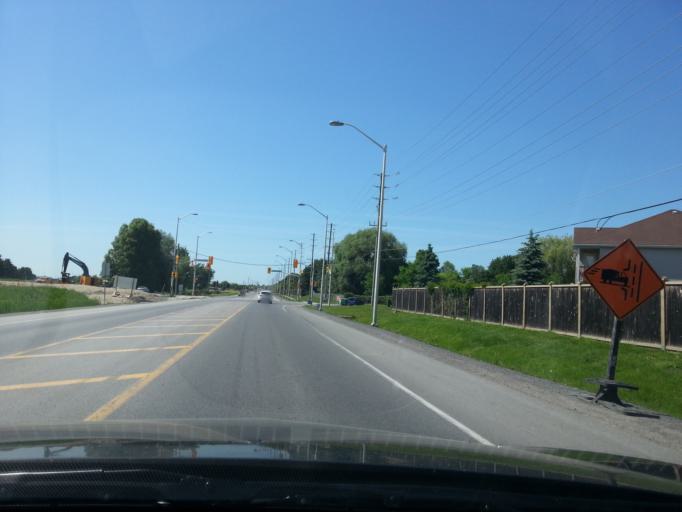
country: CA
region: Ontario
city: Bells Corners
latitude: 45.2843
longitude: -75.8848
